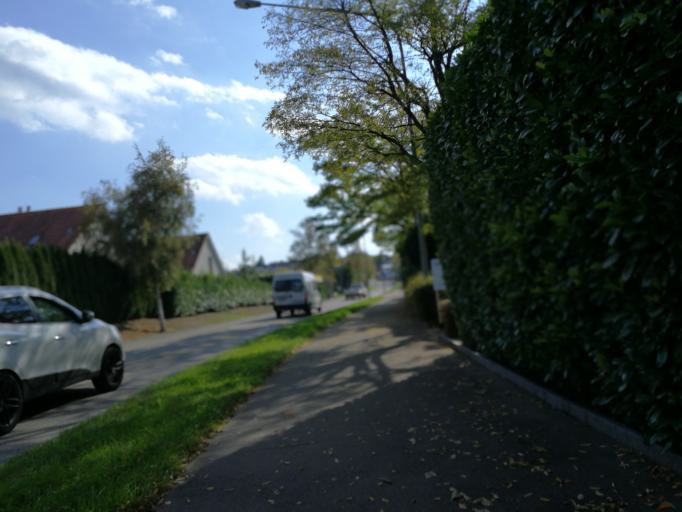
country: CH
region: Zurich
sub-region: Bezirk Meilen
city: Oetwil am See
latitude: 47.2760
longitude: 8.7189
